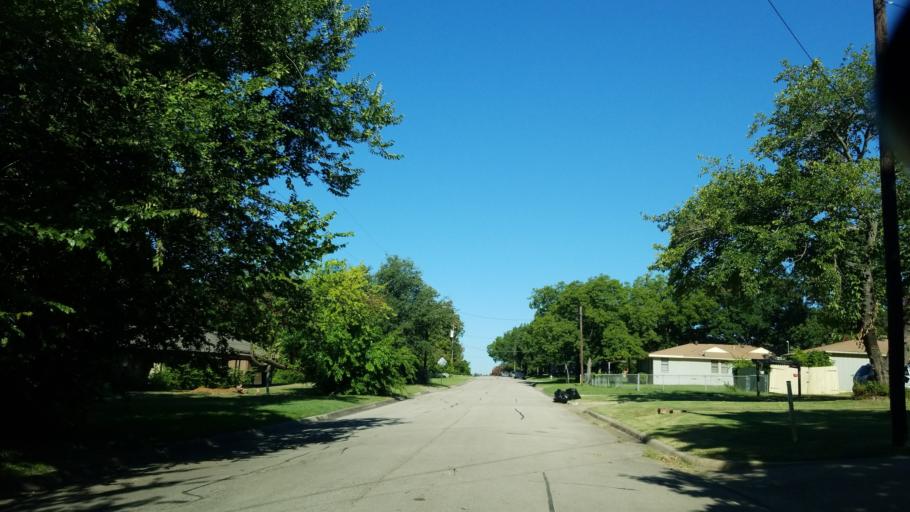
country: US
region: Texas
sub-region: Dallas County
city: Carrollton
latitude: 32.9507
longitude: -96.8990
